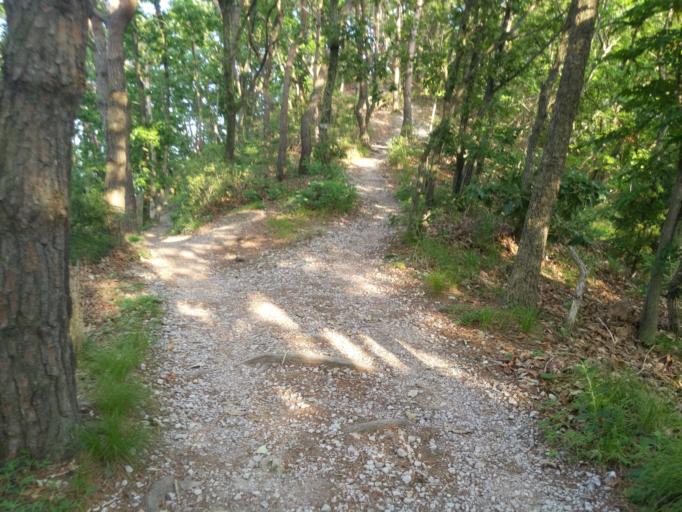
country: KR
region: Daegu
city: Hwawon
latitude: 35.7830
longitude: 128.5467
